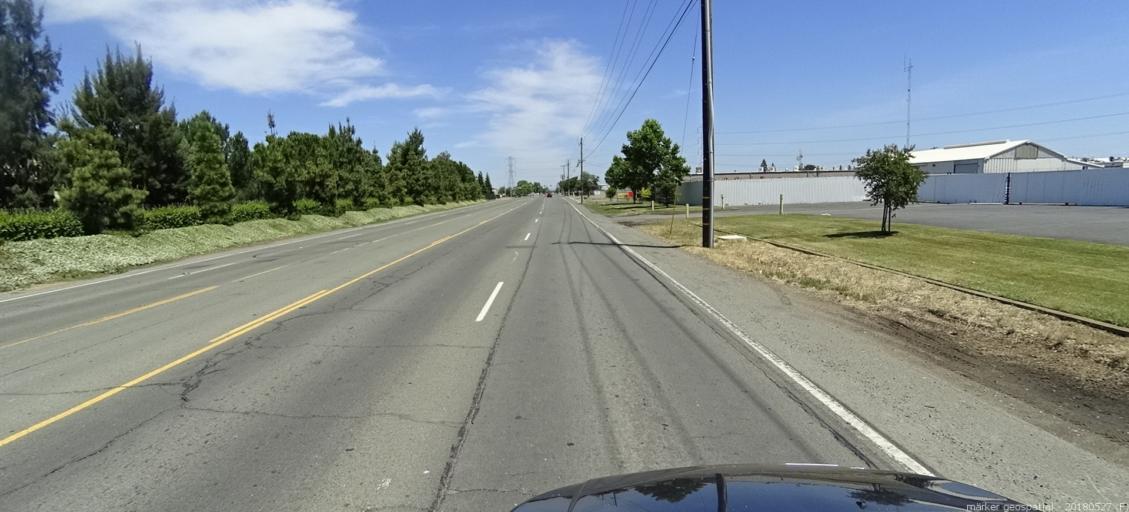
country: US
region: California
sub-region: Sacramento County
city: Florin
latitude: 38.5219
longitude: -121.3906
